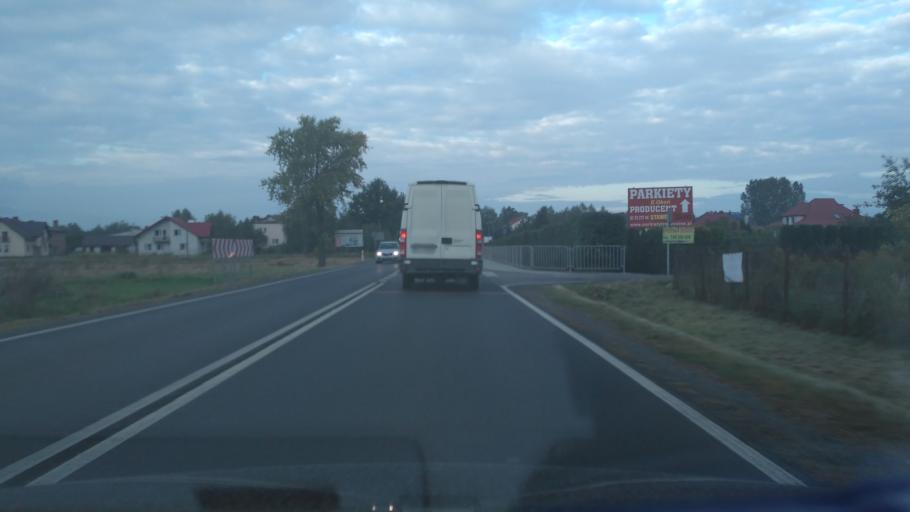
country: PL
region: Lublin Voivodeship
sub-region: Powiat leczynski
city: Spiczyn
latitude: 51.2980
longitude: 22.7190
